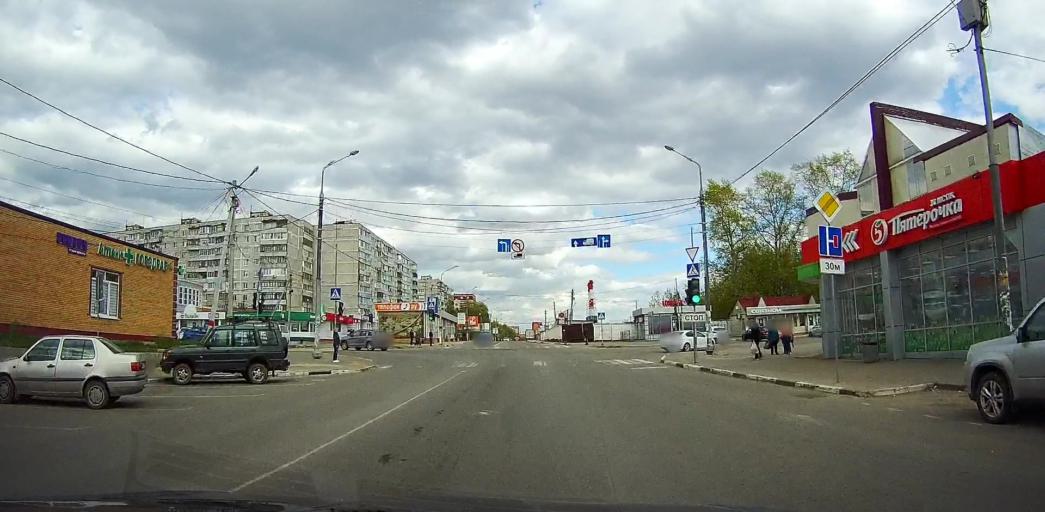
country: RU
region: Moskovskaya
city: Pavlovskiy Posad
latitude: 55.7757
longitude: 38.6510
